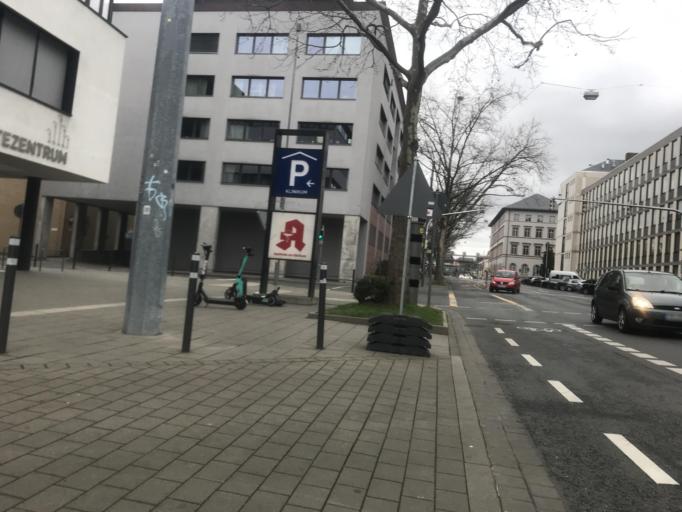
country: DE
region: Hesse
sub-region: Regierungsbezirk Darmstadt
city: Darmstadt
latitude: 49.8735
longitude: 8.6485
